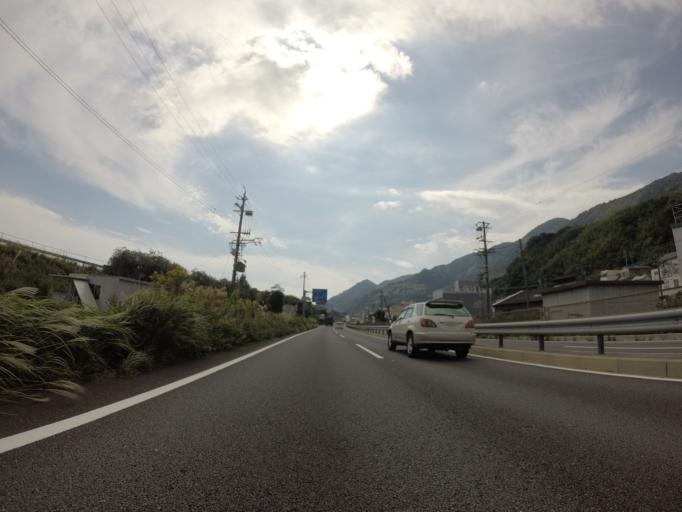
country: JP
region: Shizuoka
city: Fujinomiya
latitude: 35.0986
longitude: 138.5545
